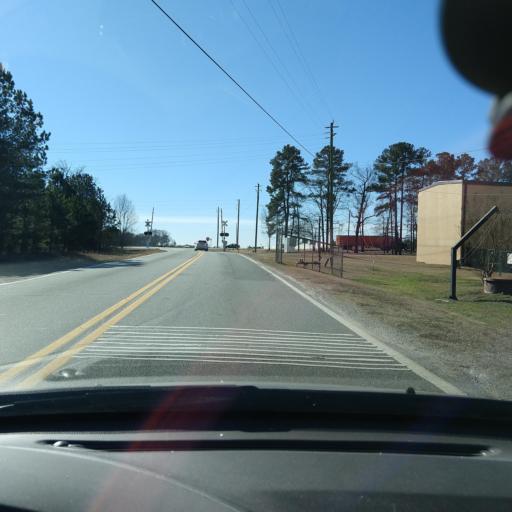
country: US
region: Georgia
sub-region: Walton County
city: Social Circle
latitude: 33.6533
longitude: -83.6903
